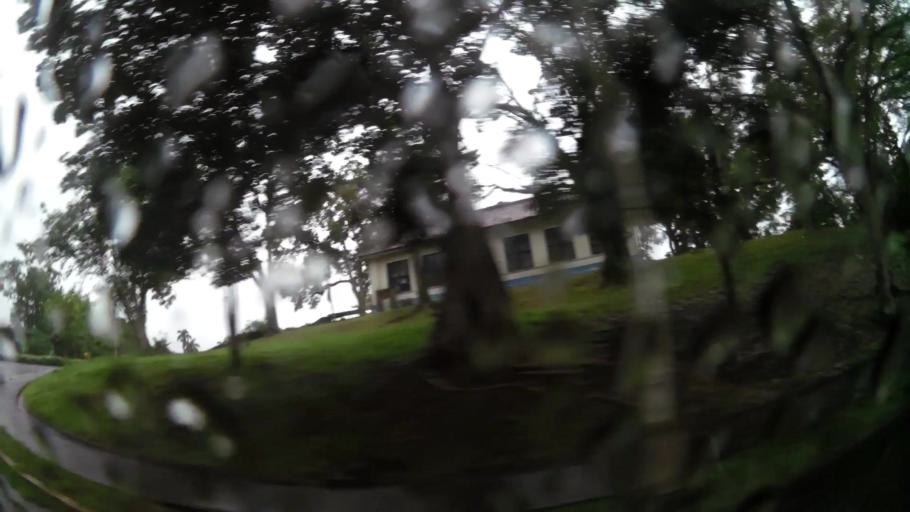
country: PA
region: Panama
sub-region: Distrito de Panama
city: Paraiso
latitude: 9.0214
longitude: -79.6109
